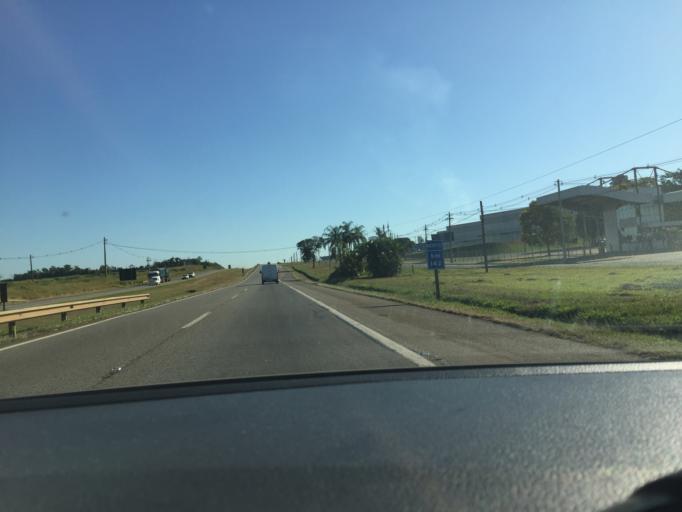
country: BR
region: Sao Paulo
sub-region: Santo Antonio De Posse
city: Santo Antonio de Posse
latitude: -22.6062
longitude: -47.0073
